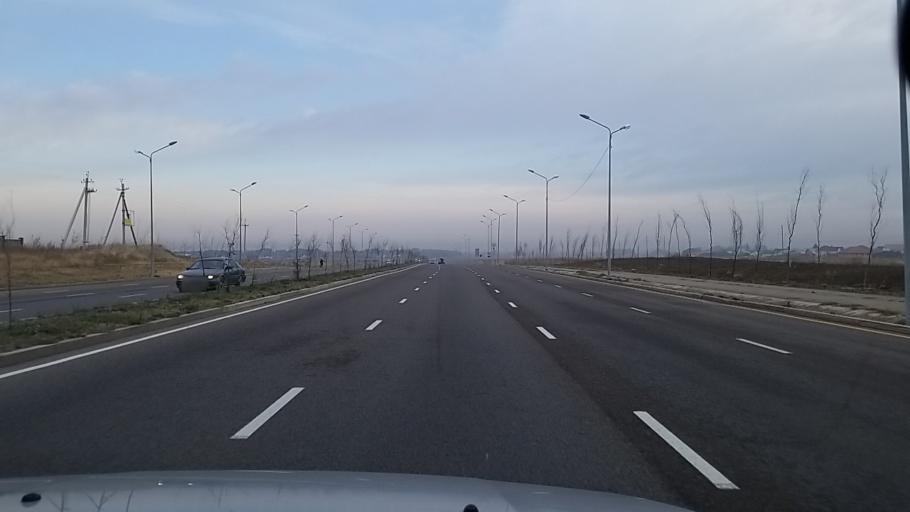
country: KZ
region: Almaty Oblysy
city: Burunday
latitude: 43.3402
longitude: 76.8337
